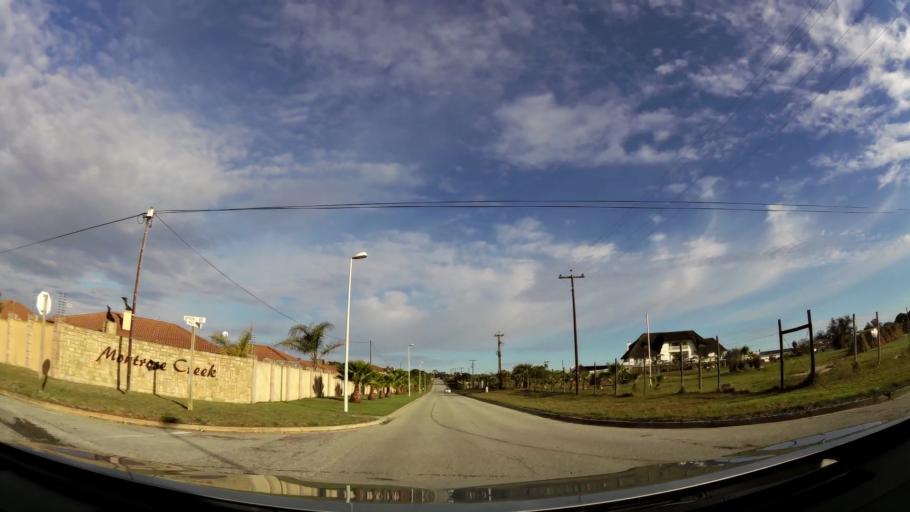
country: ZA
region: Eastern Cape
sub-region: Nelson Mandela Bay Metropolitan Municipality
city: Port Elizabeth
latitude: -33.9537
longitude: 25.4876
